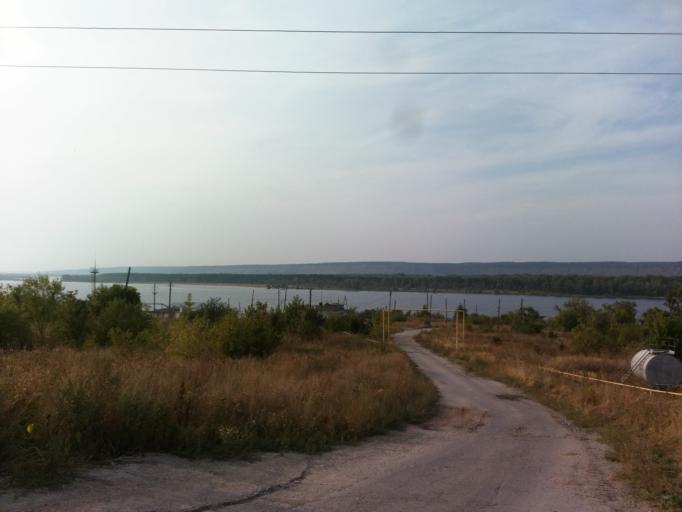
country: RU
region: Samara
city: Pribrezhnyy
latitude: 53.4400
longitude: 49.7484
